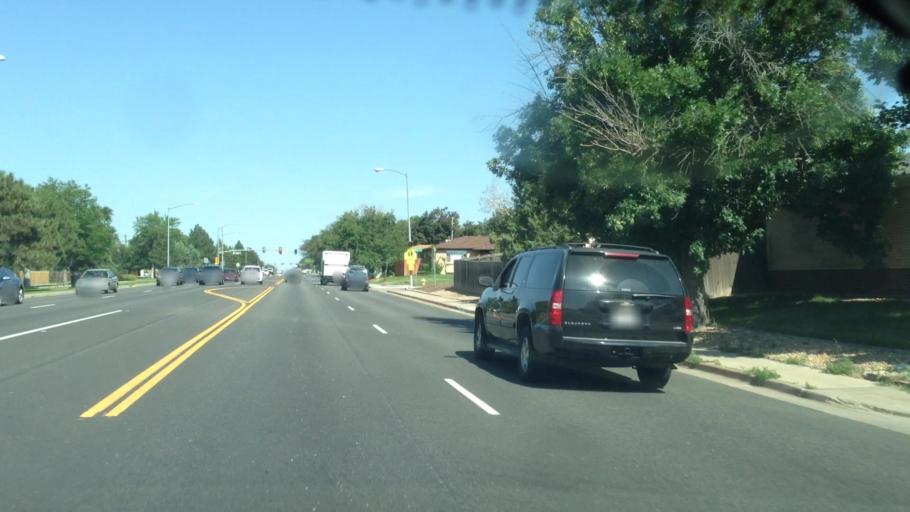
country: US
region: Colorado
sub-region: Adams County
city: Aurora
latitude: 39.7255
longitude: -104.8735
